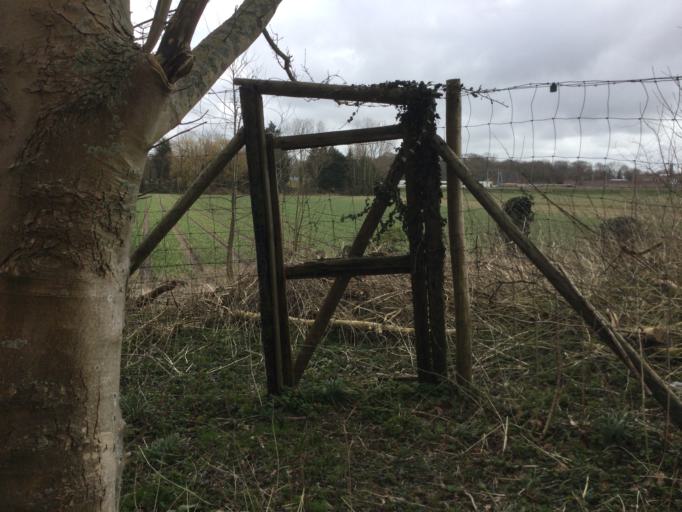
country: NL
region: North Holland
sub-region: Gemeente Bloemendaal
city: Bennebroek
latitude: 52.3325
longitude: 4.5883
